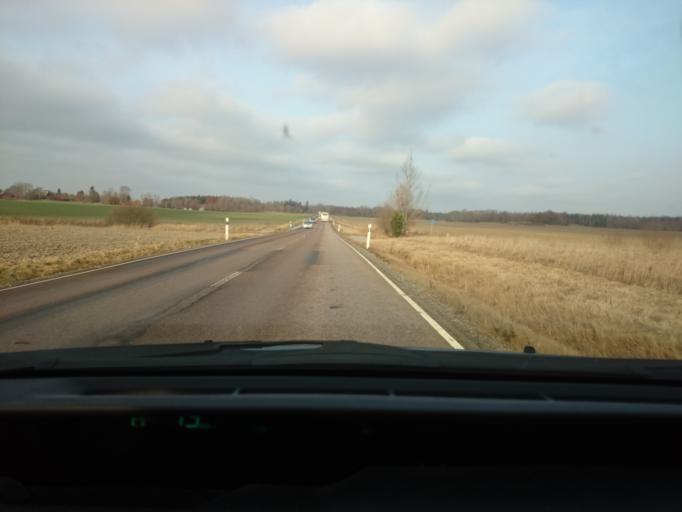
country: SE
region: Vaestmanland
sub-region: Vasteras
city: Vasteras
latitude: 59.6554
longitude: 16.4924
